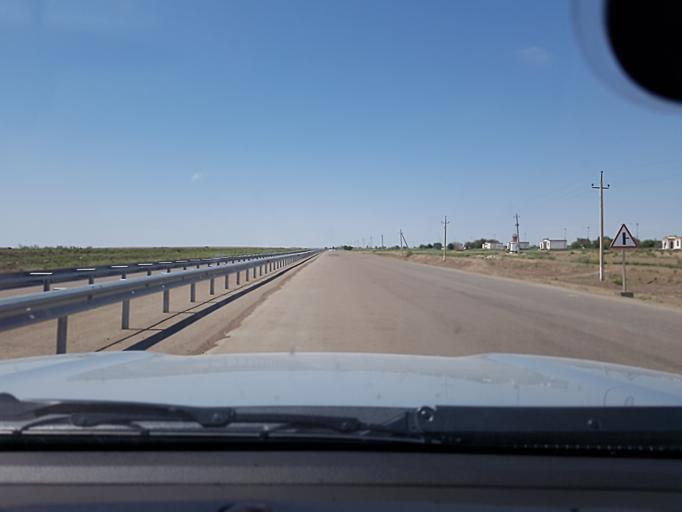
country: TM
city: Akdepe
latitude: 41.7404
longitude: 59.2340
